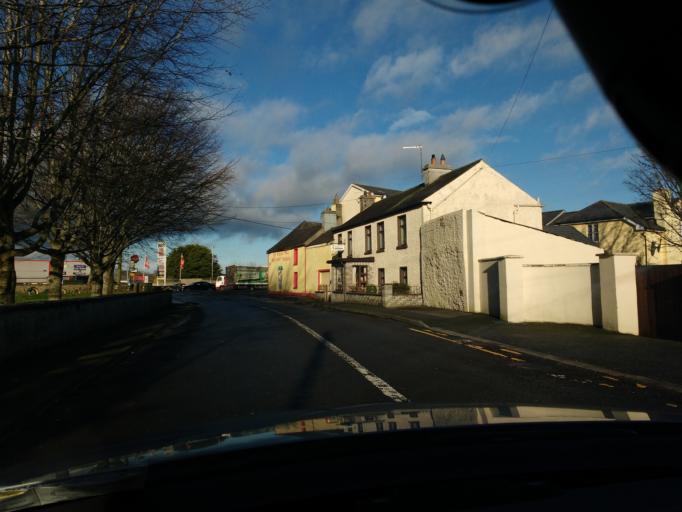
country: IE
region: Leinster
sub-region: Laois
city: Rathdowney
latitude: 52.7187
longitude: -7.5846
